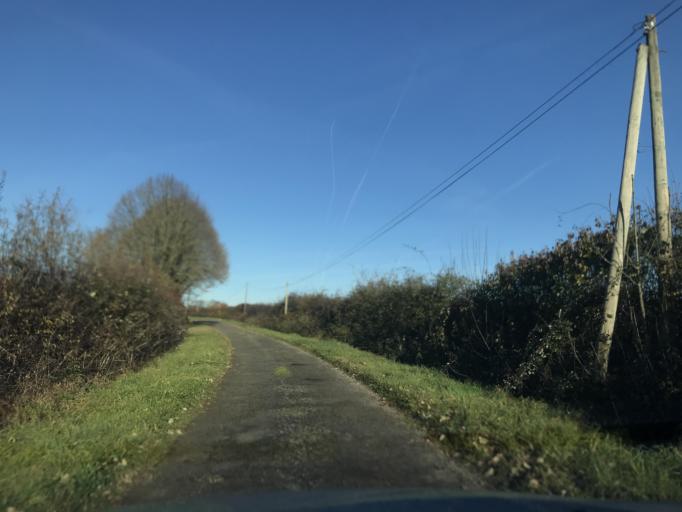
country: FR
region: Poitou-Charentes
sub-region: Departement de la Charente
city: Saint-Claud
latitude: 45.8532
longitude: 0.5149
